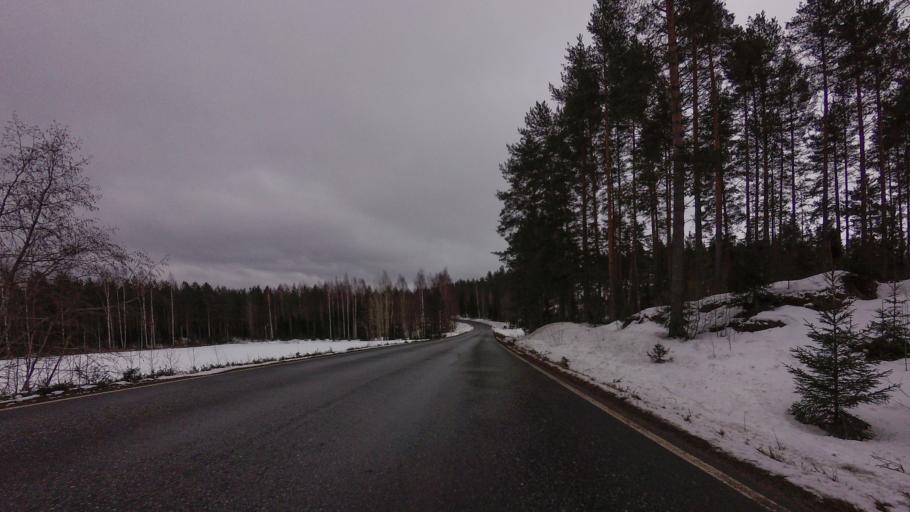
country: FI
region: Southern Savonia
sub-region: Savonlinna
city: Savonlinna
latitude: 61.9862
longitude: 28.7915
